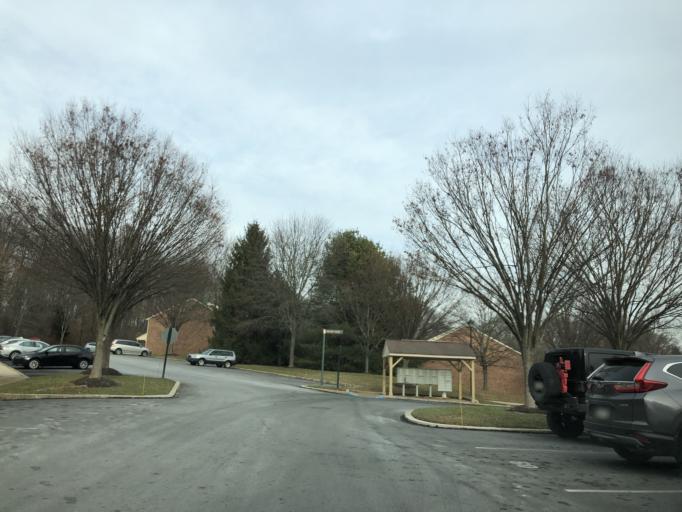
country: US
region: Pennsylvania
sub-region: Chester County
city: Exton
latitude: 40.0326
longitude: -75.6375
